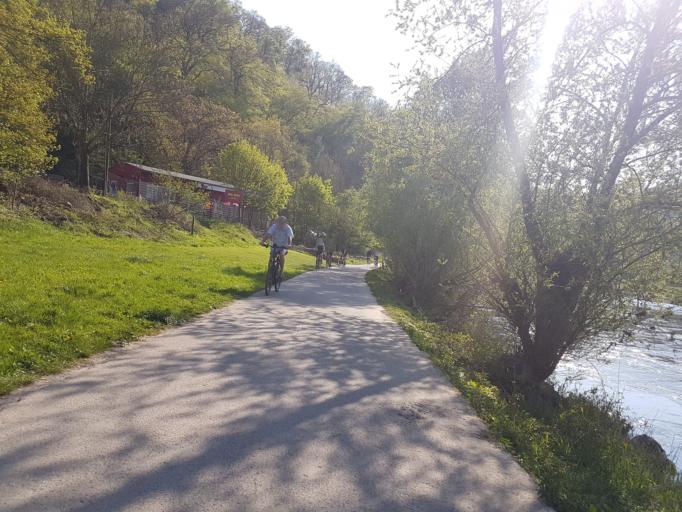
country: DE
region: North Rhine-Westphalia
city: Hattingen
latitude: 51.3881
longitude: 7.1619
